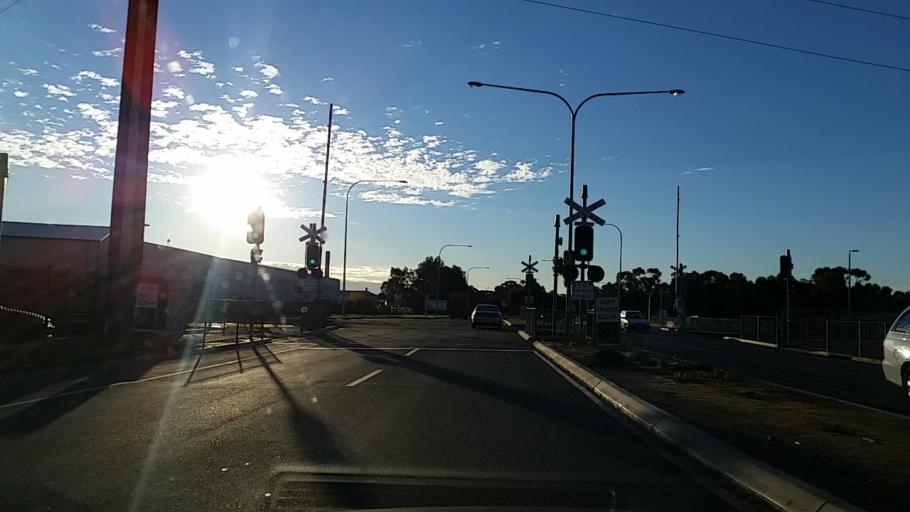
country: AU
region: South Australia
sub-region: Salisbury
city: Salisbury
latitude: -34.7511
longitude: 138.6445
